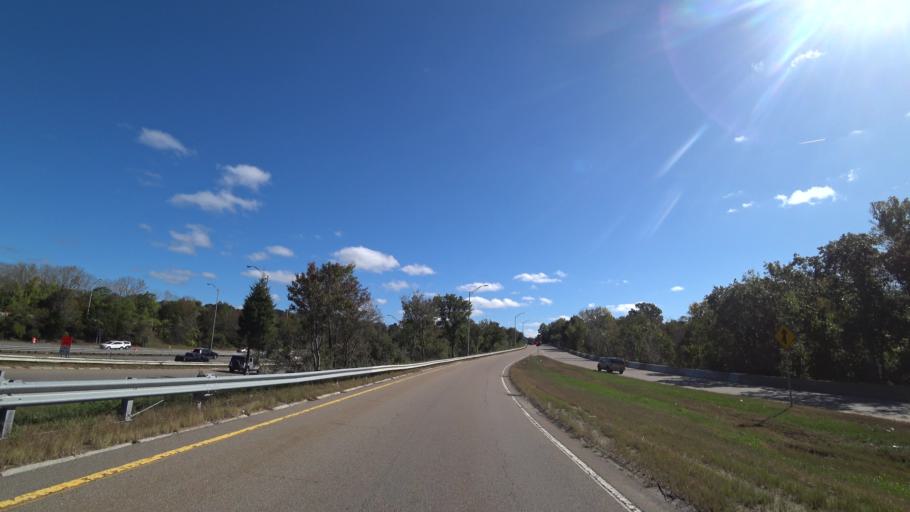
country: US
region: Massachusetts
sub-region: Norfolk County
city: Braintree
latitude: 42.2270
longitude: -71.0080
